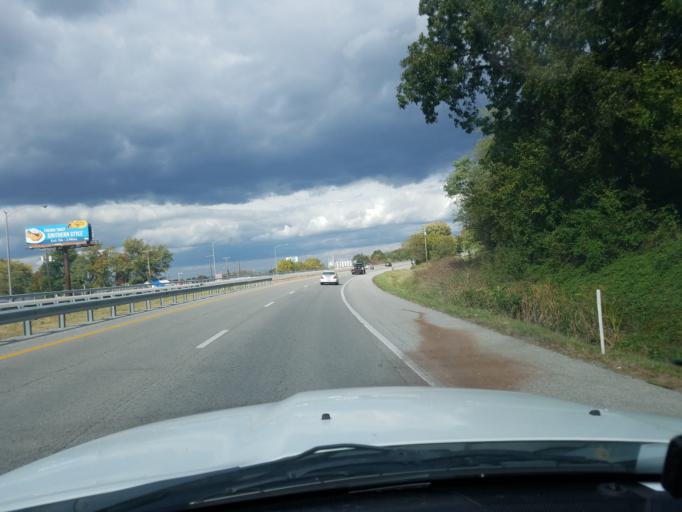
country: US
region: Kentucky
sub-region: Henderson County
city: Henderson
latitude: 37.8272
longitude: -87.5664
